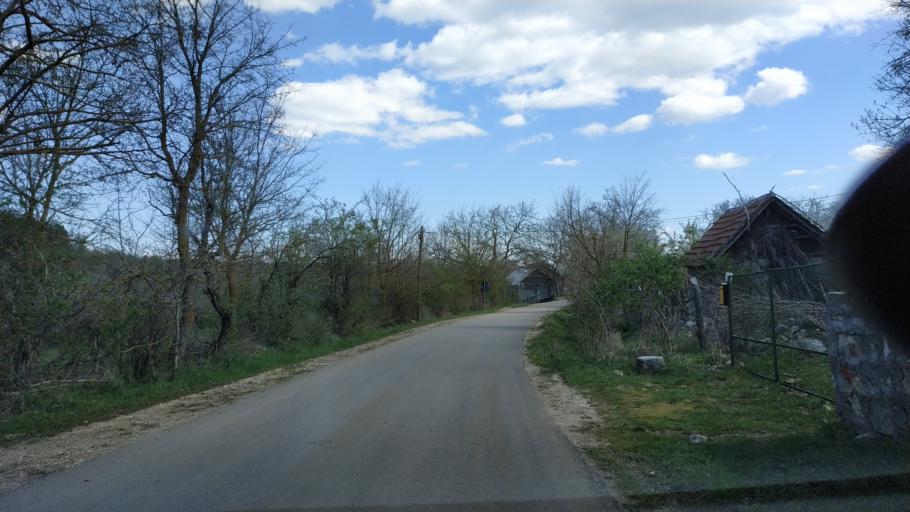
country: RS
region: Central Serbia
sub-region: Zajecarski Okrug
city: Soko Banja
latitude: 43.5740
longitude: 21.8982
